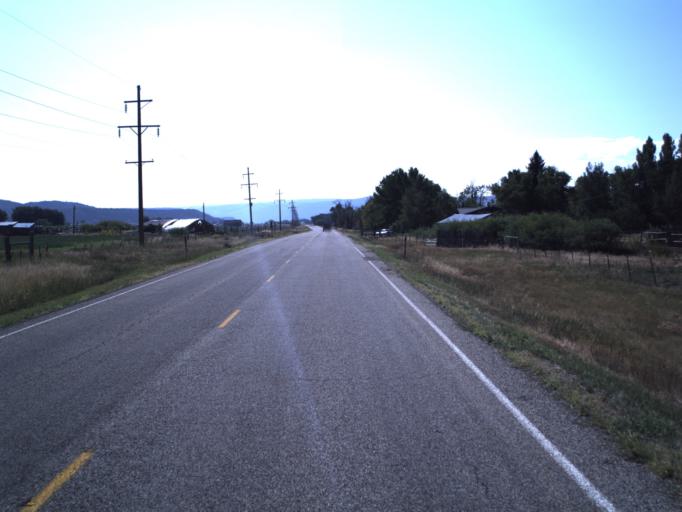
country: US
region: Utah
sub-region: Duchesne County
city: Duchesne
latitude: 40.3838
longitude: -110.7415
